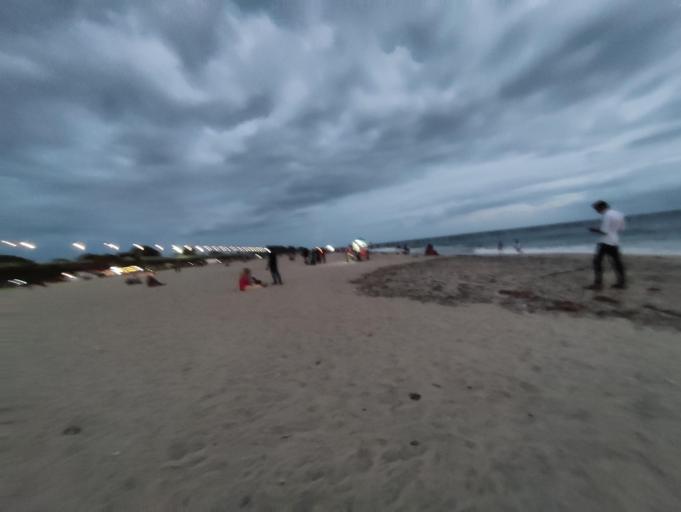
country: IN
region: Kerala
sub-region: Alappuzha
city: Alleppey
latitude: 9.4941
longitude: 76.3170
